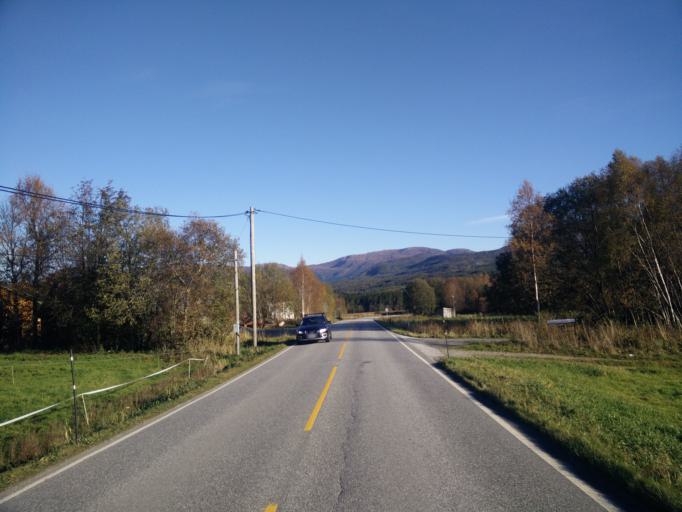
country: NO
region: More og Romsdal
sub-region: Halsa
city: Liaboen
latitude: 63.0724
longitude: 8.2636
